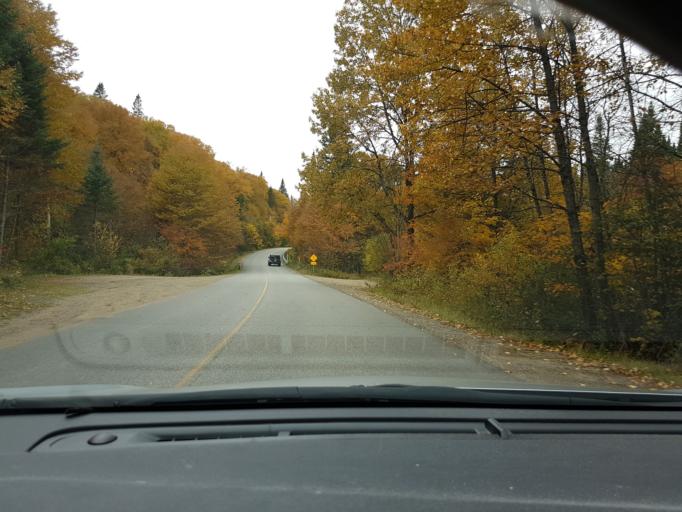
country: CA
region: Quebec
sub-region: Capitale-Nationale
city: Shannon
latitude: 47.1110
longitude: -71.3486
